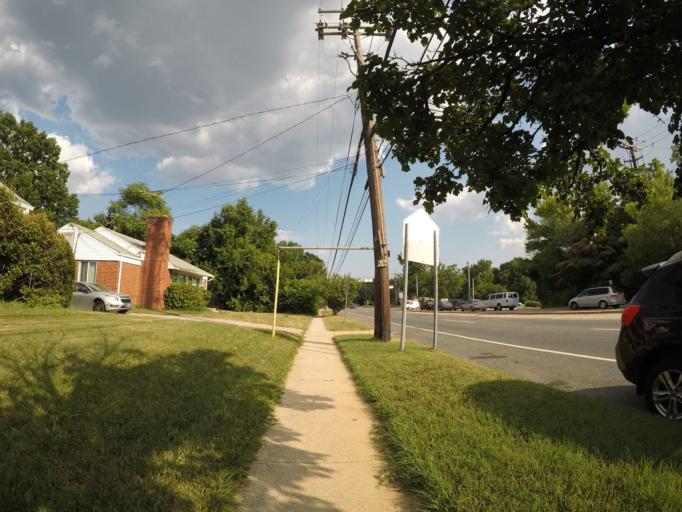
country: US
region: Maryland
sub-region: Prince George's County
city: University Park
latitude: 38.9746
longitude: -76.9512
